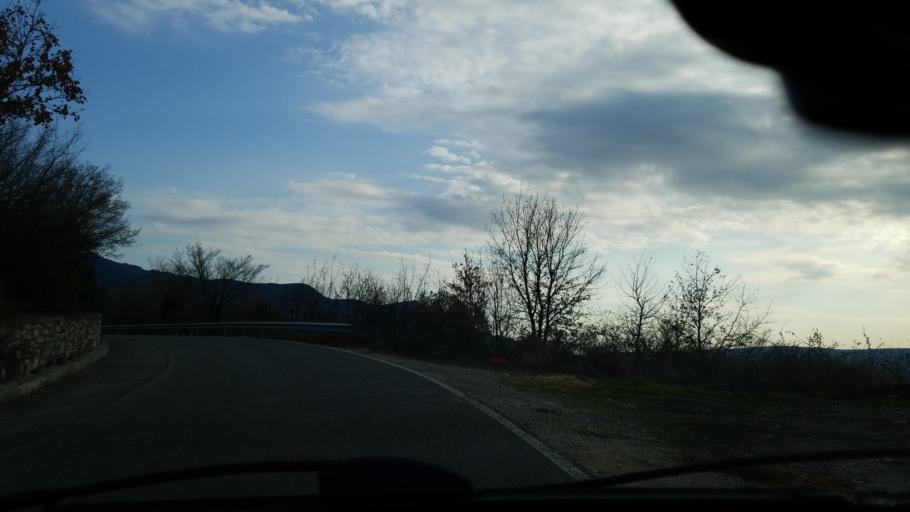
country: AL
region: Lezhe
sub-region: Rrethi i Lezhes
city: Kallmeti i Madh
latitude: 41.8754
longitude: 19.6950
